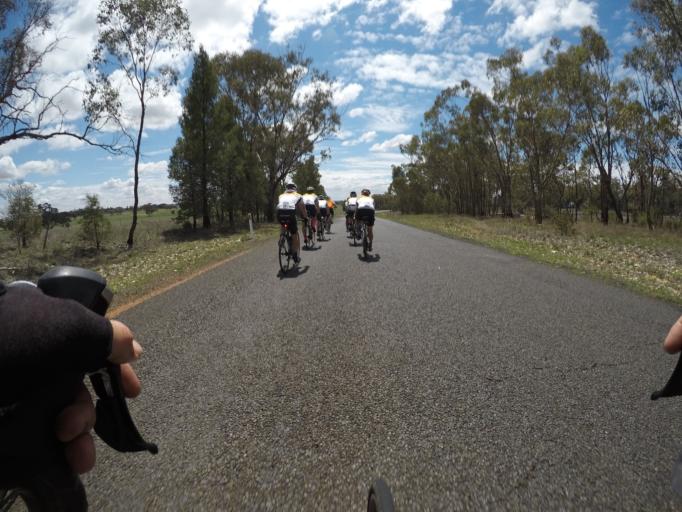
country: AU
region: New South Wales
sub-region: Dubbo Municipality
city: Dubbo
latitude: -32.3686
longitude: 148.5820
